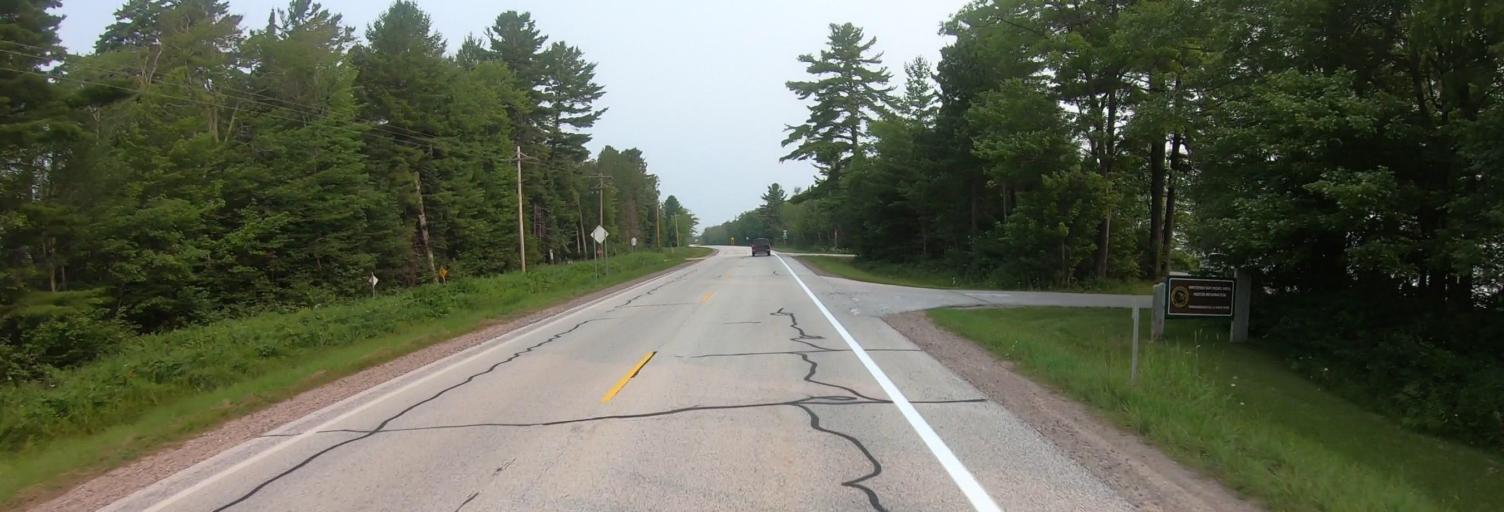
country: US
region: Michigan
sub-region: Luce County
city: Newberry
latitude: 46.5624
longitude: -85.0295
